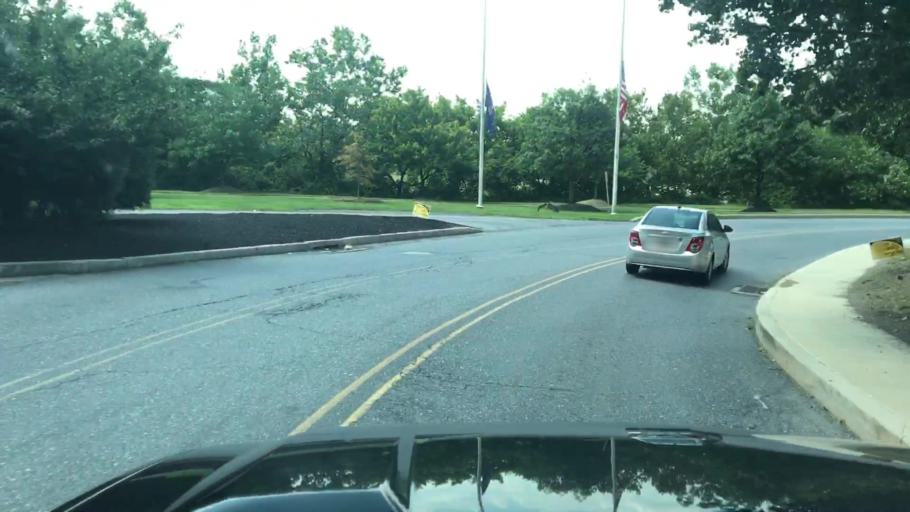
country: US
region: Pennsylvania
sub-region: Cumberland County
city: New Cumberland
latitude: 40.2479
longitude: -76.8697
